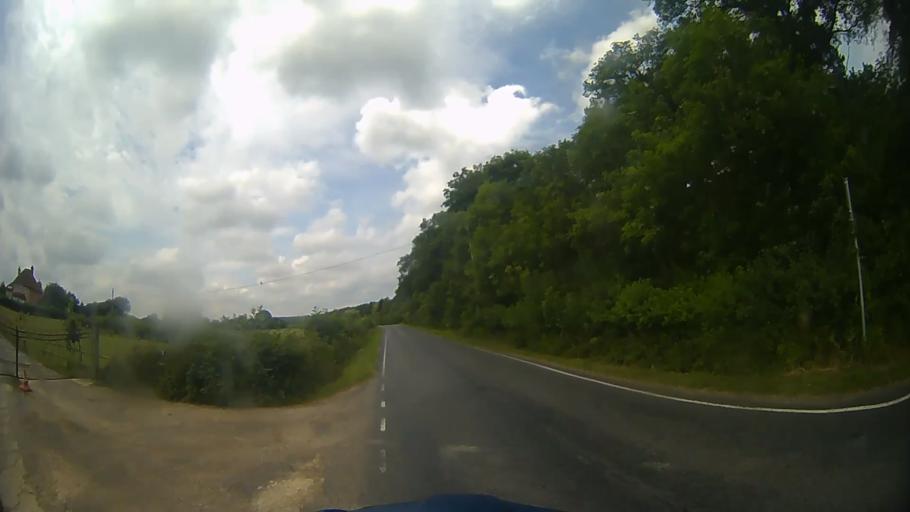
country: GB
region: England
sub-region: Hampshire
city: Kingsley
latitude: 51.1585
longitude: -0.8522
